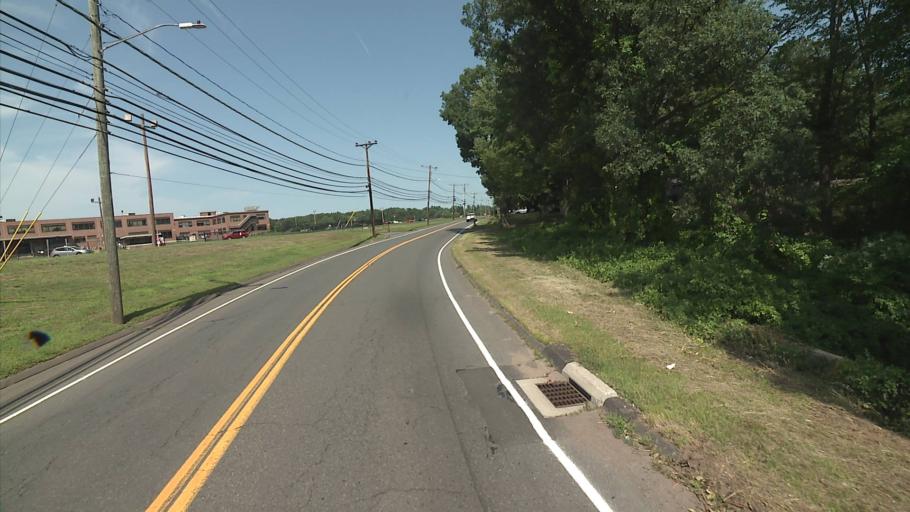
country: US
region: Connecticut
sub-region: Hartford County
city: Blue Hills
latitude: 41.8590
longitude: -72.7007
